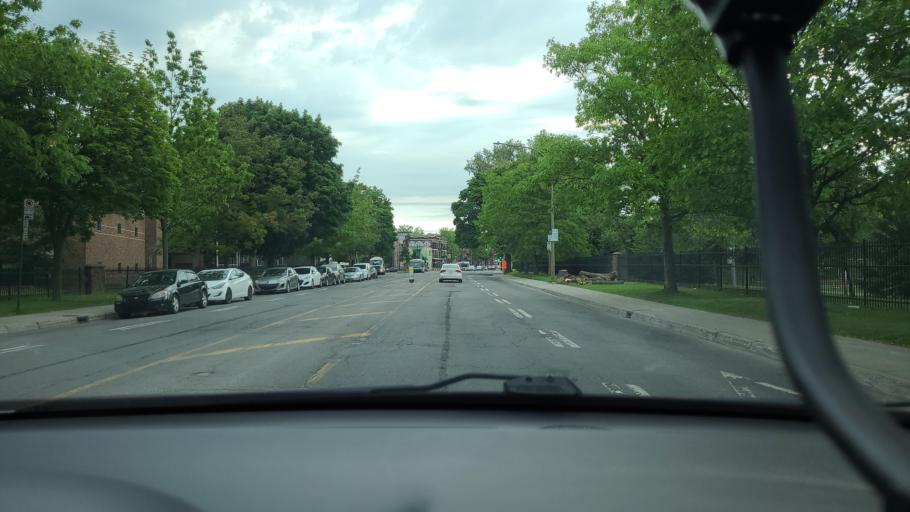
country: CA
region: Quebec
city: Montreal-Ouest
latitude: 45.4584
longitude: -73.6382
